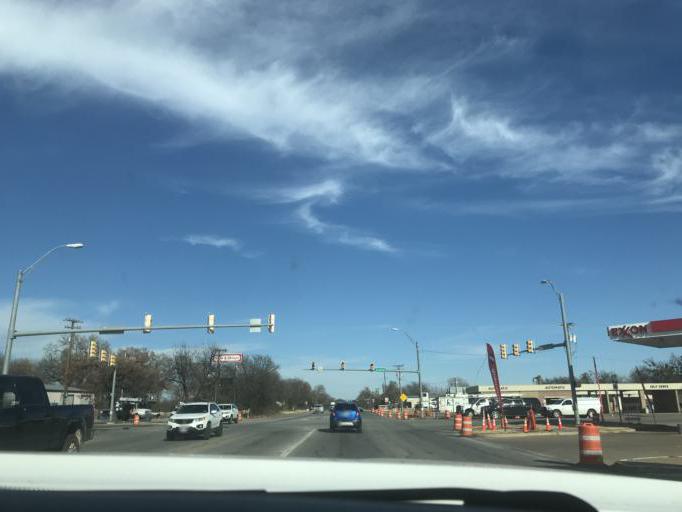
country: US
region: Texas
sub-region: Erath County
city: Stephenville
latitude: 32.2319
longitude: -98.2106
